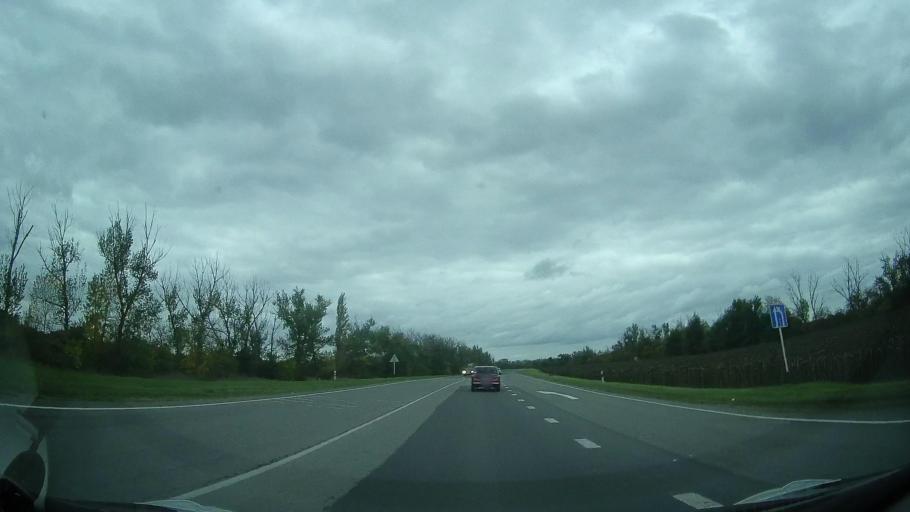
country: RU
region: Rostov
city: Yegorlykskaya
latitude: 46.5391
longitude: 40.7769
